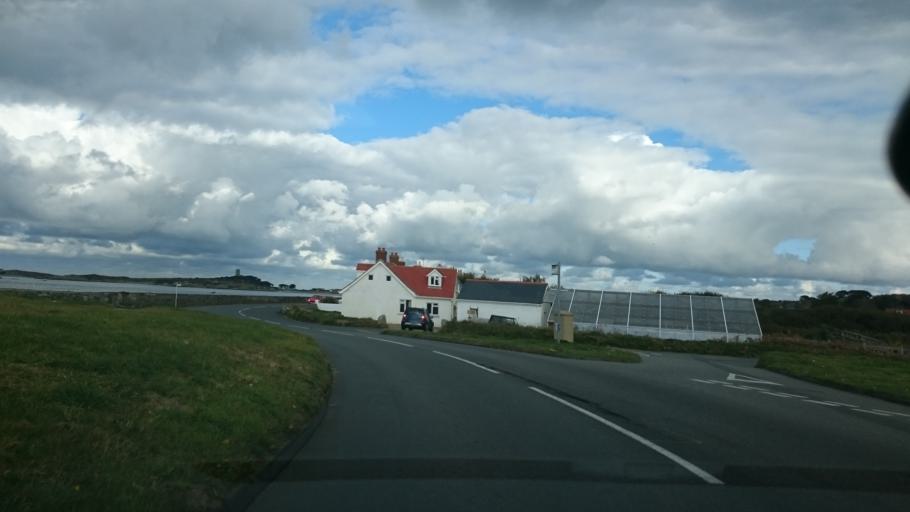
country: GG
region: St Peter Port
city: Saint Peter Port
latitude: 49.4442
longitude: -2.6490
